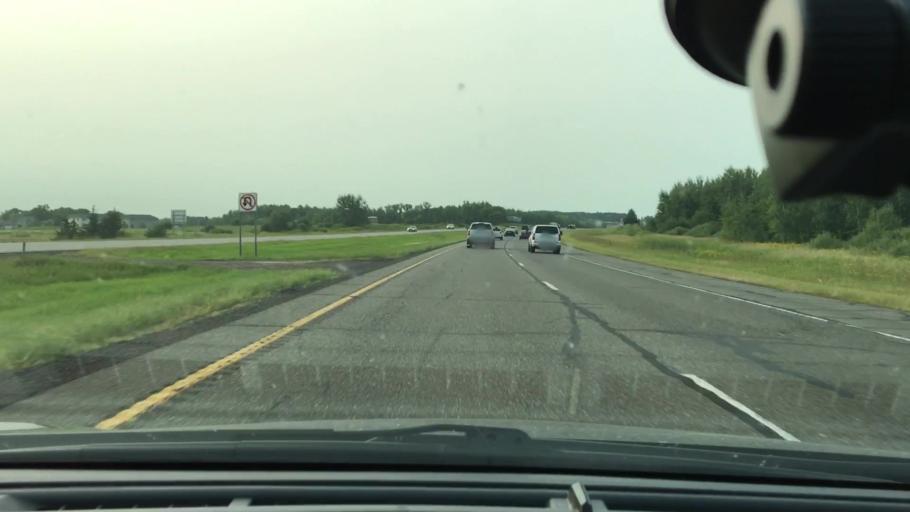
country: US
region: Minnesota
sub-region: Mille Lacs County
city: Milaca
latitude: 45.7670
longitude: -93.6432
